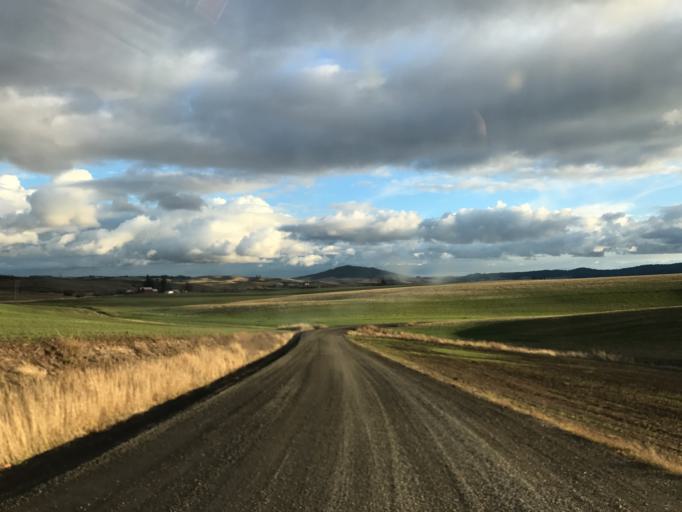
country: US
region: Idaho
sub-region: Latah County
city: Moscow
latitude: 46.7702
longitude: -116.9806
